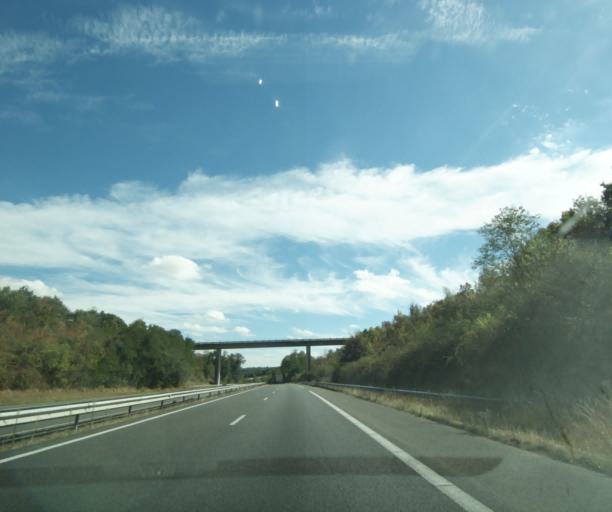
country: FR
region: Midi-Pyrenees
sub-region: Departement du Tarn-et-Garonne
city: Lamagistere
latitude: 44.0783
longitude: 0.8002
